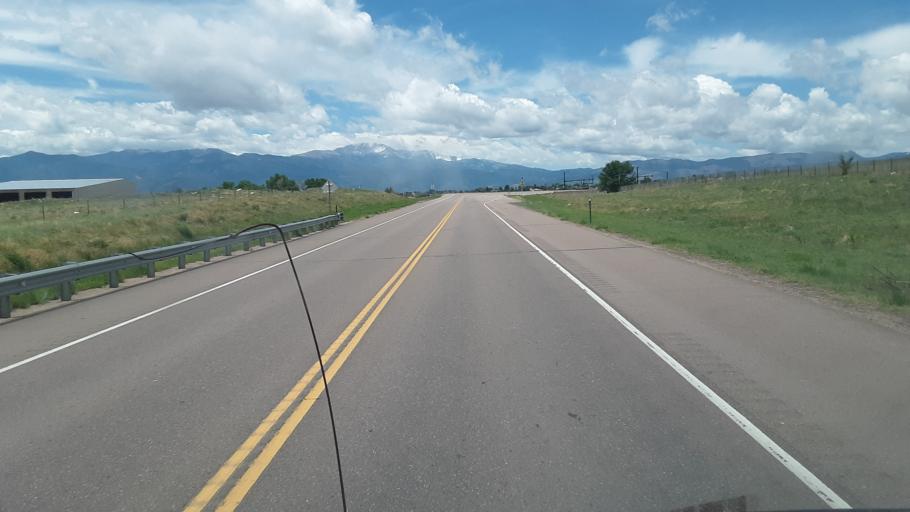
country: US
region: Colorado
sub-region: El Paso County
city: Cimarron Hills
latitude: 38.8418
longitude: -104.6856
